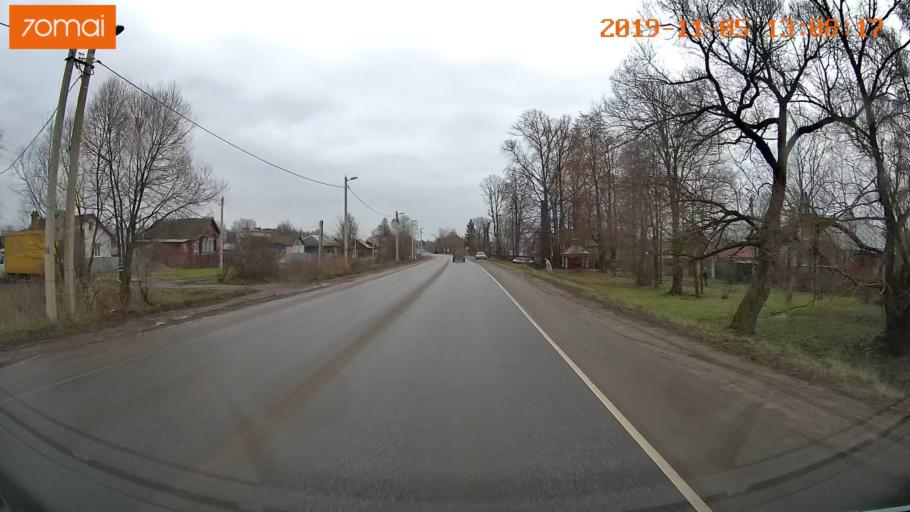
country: RU
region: Ivanovo
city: Kitovo
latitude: 56.8645
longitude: 41.2895
